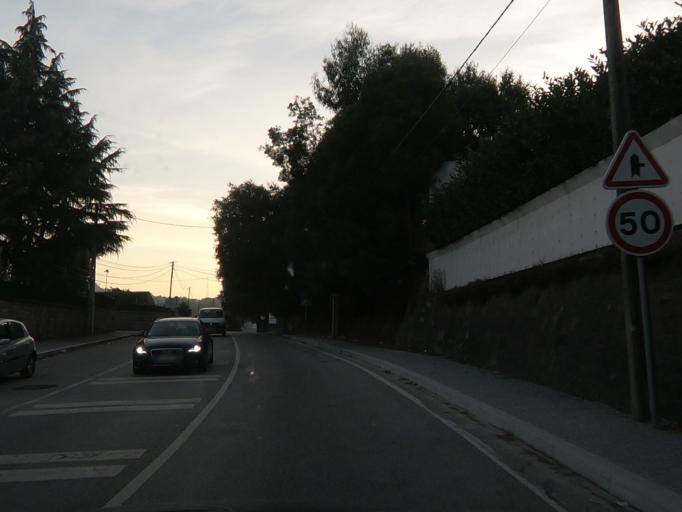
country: PT
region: Porto
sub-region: Gondomar
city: Valbom
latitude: 41.1267
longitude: -8.5602
